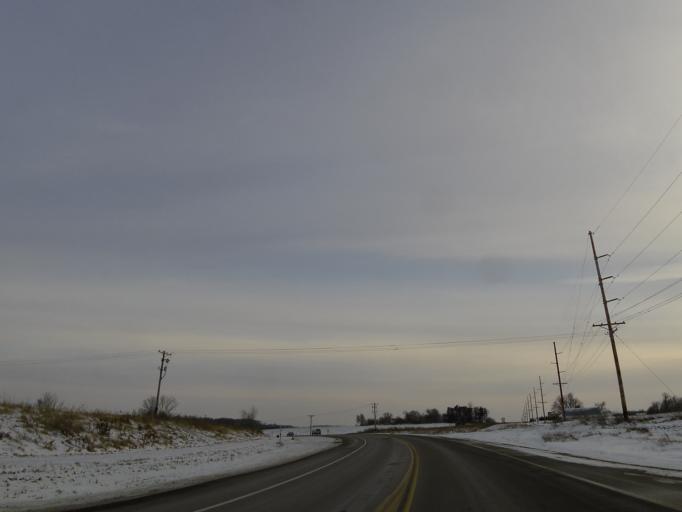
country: US
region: Minnesota
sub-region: Carver County
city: Carver
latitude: 44.8062
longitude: -93.6525
